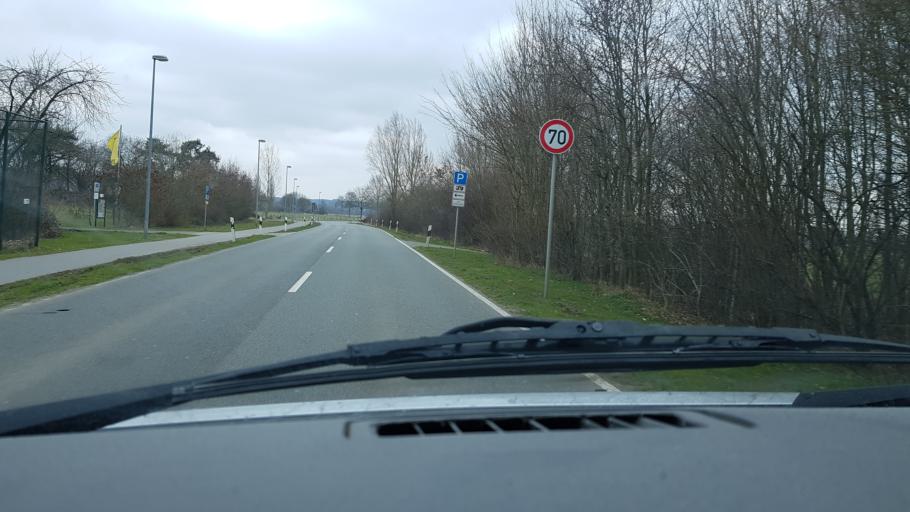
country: DE
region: North Rhine-Westphalia
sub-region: Regierungsbezirk Dusseldorf
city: Kranenburg
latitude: 51.7925
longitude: 6.0115
